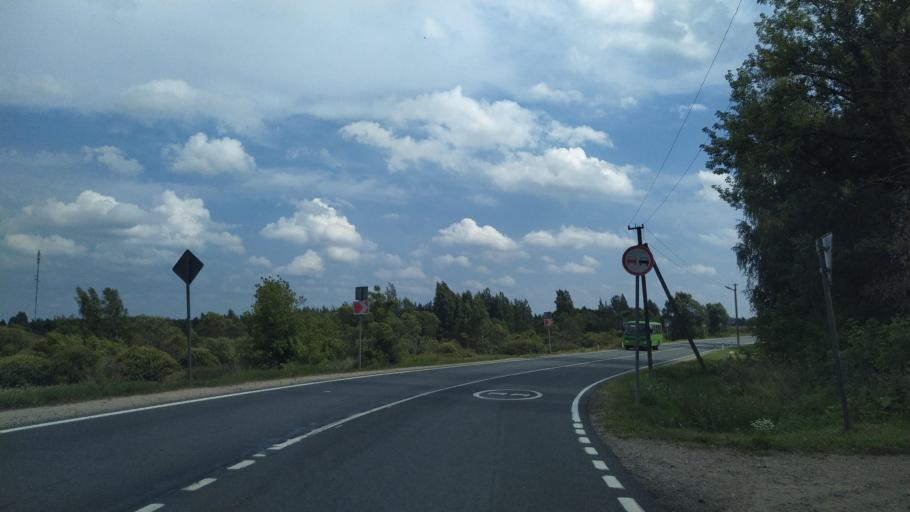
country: RU
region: Pskov
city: Pskov
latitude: 57.7605
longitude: 28.7687
